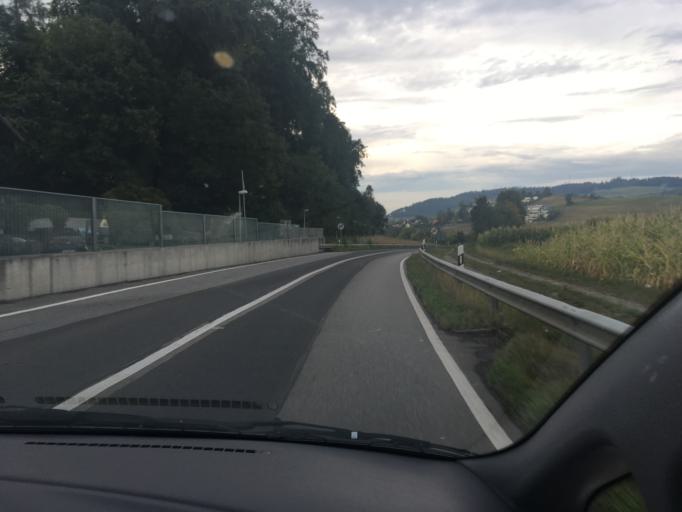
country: CH
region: Bern
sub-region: Bern-Mittelland District
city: Bolligen
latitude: 46.9611
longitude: 7.5057
